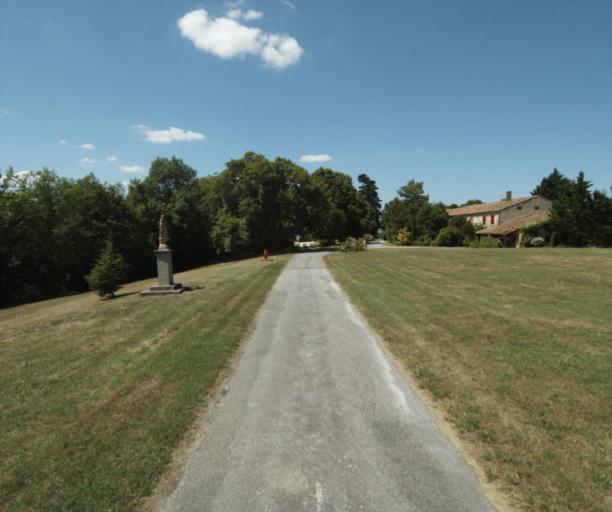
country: FR
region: Midi-Pyrenees
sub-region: Departement de la Haute-Garonne
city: Saint-Felix-Lauragais
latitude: 43.4777
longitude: 1.8606
